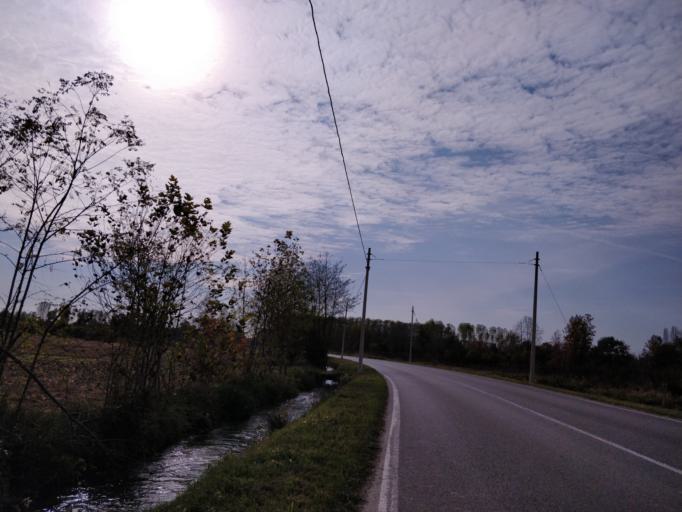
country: IT
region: Friuli Venezia Giulia
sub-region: Provincia di Udine
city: Bertiolo
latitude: 45.9293
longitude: 13.0489
